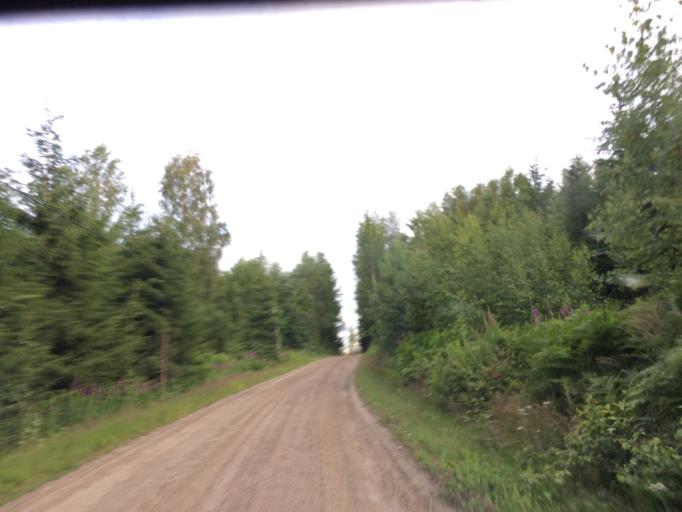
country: FI
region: Haeme
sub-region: Haemeenlinna
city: Janakkala
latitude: 60.8852
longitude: 24.6104
